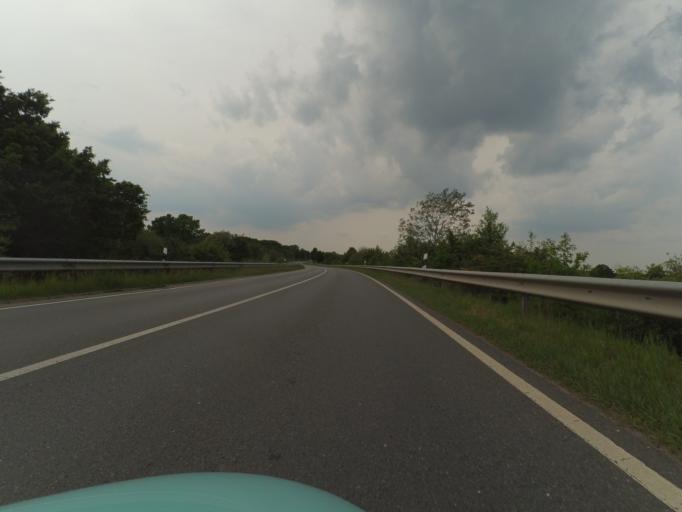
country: DE
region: Lower Saxony
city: Arpke
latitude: 52.3957
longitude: 10.0979
